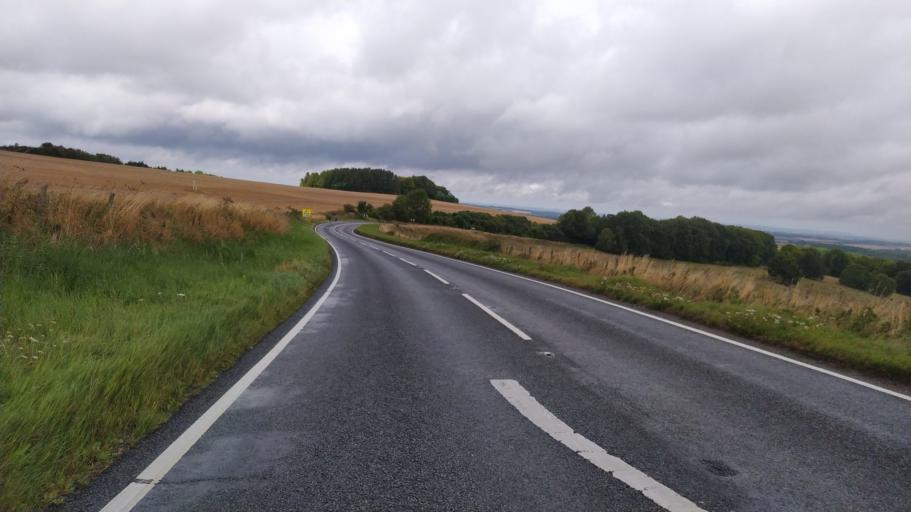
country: GB
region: England
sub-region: Hampshire
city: Kings Worthy
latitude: 51.0473
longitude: -1.2482
